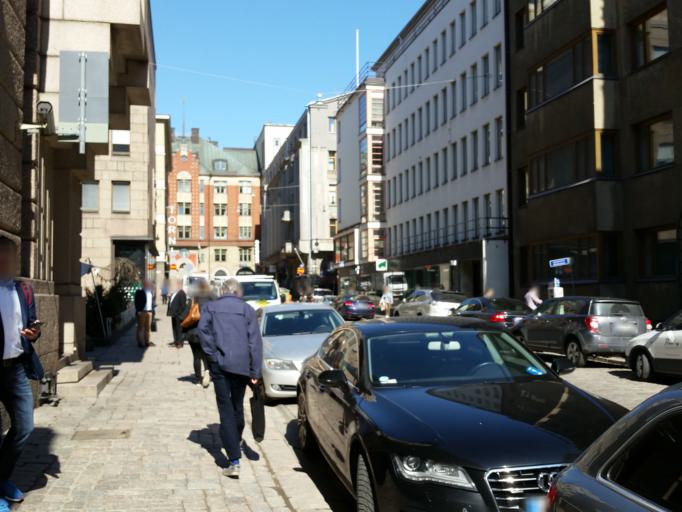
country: FI
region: Uusimaa
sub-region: Helsinki
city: Helsinki
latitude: 60.1673
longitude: 24.9399
